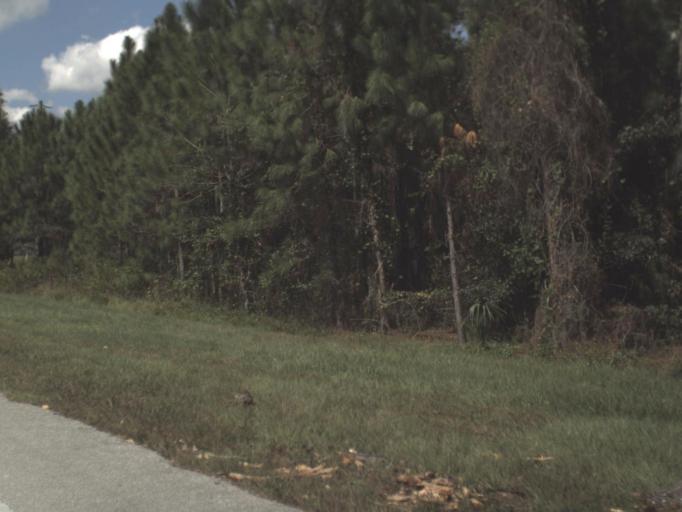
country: US
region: Florida
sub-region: Hardee County
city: Zolfo Springs
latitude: 27.4545
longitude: -81.6482
